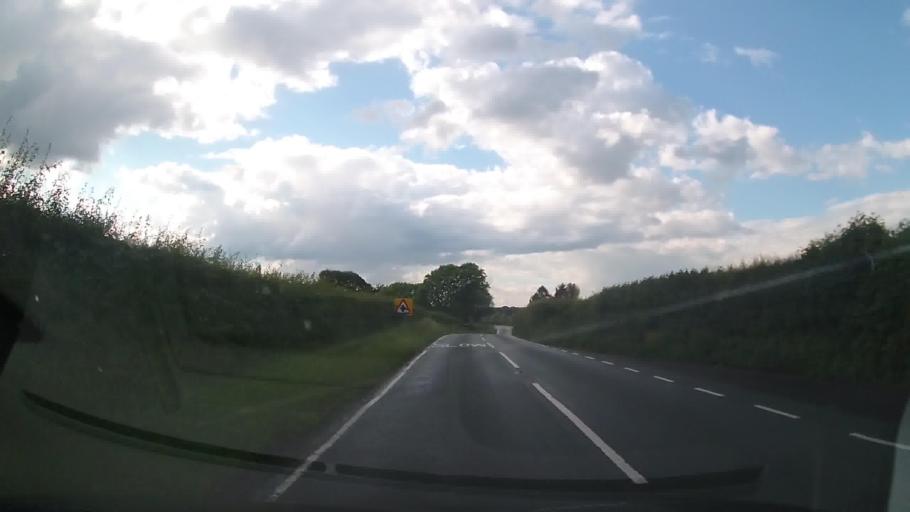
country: GB
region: England
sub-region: Shropshire
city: Withington
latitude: 52.6737
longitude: -2.6426
